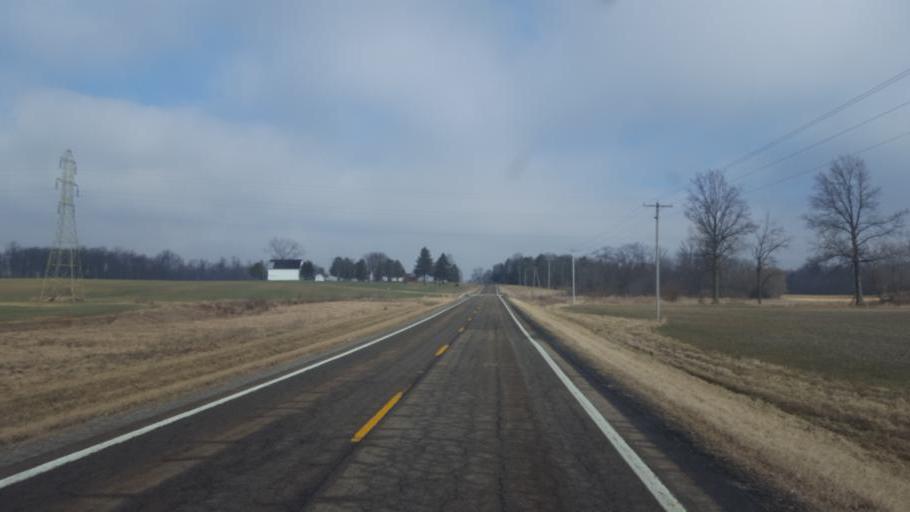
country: US
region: Ohio
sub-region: Crawford County
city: Galion
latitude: 40.6846
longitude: -82.8608
